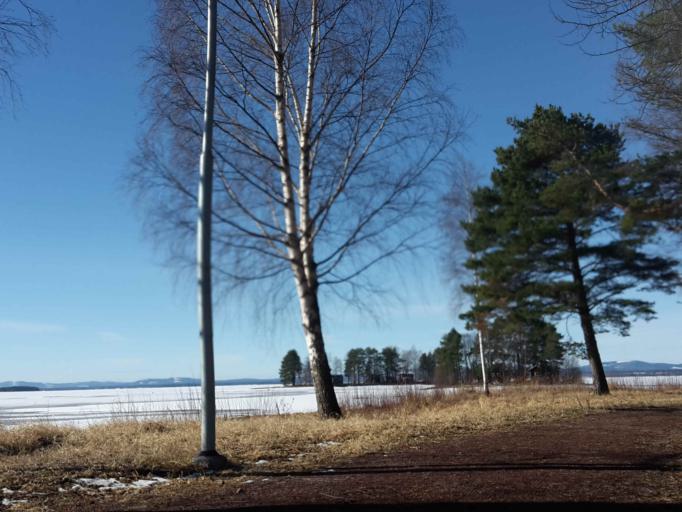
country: SE
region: Dalarna
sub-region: Orsa Kommun
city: Orsa
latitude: 61.1175
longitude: 14.6042
